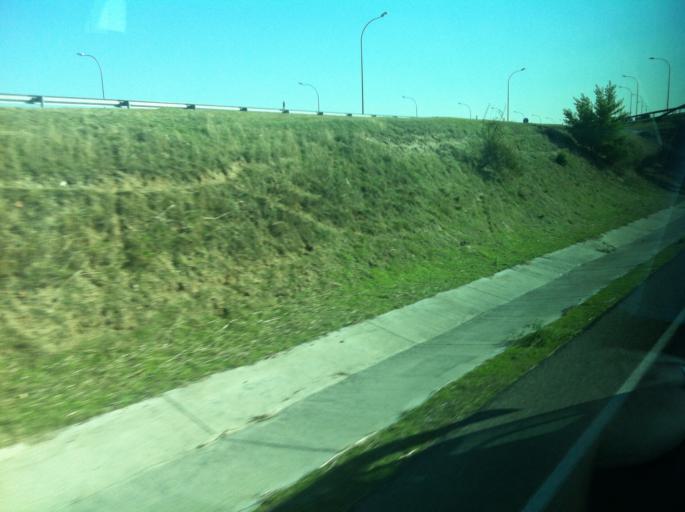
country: ES
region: Madrid
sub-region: Provincia de Madrid
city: Barajas de Madrid
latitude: 40.4937
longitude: -3.6025
